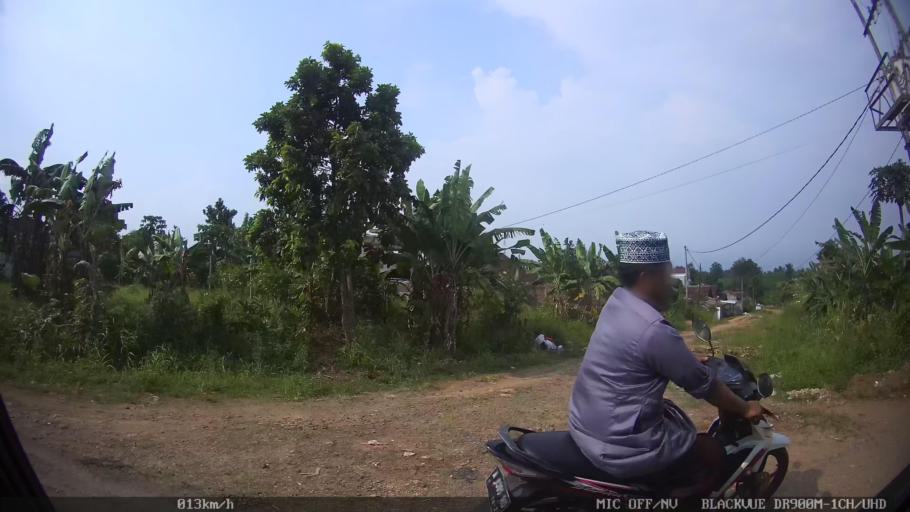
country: ID
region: Lampung
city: Kedaton
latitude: -5.3613
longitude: 105.2151
